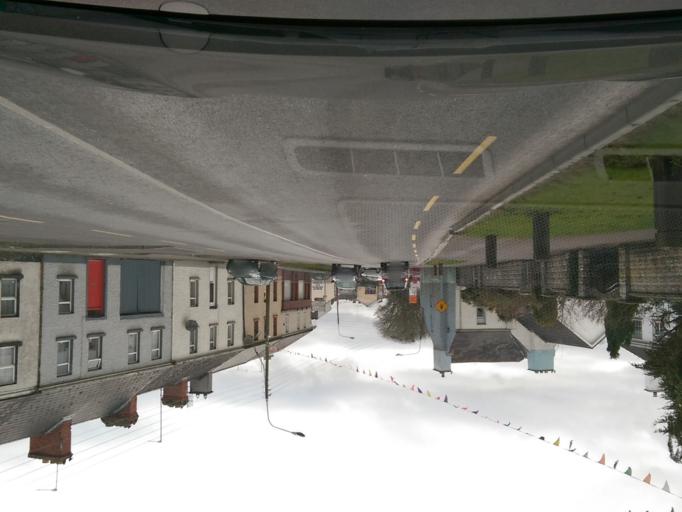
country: IE
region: Leinster
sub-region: An Iarmhi
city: Moate
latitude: 53.3952
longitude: -7.7140
